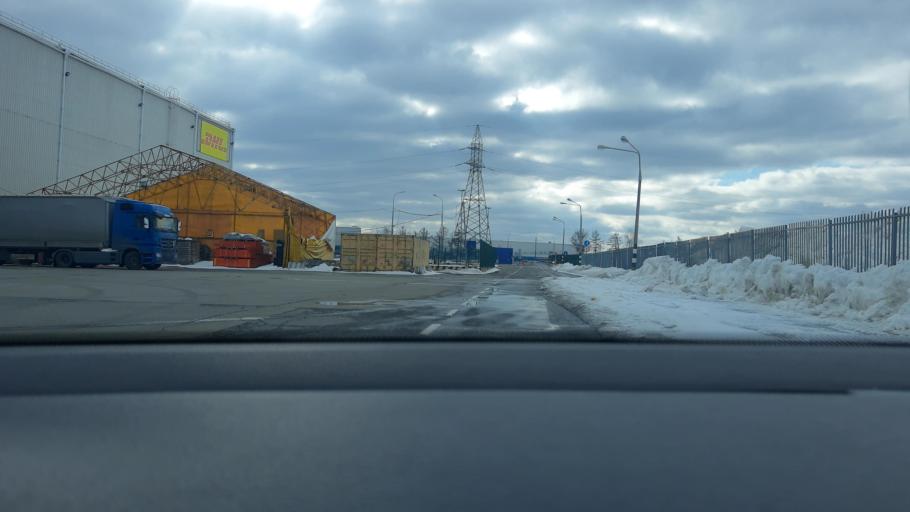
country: RU
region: Moskovskaya
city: Lesnyye Polyany
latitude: 55.9792
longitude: 37.8692
